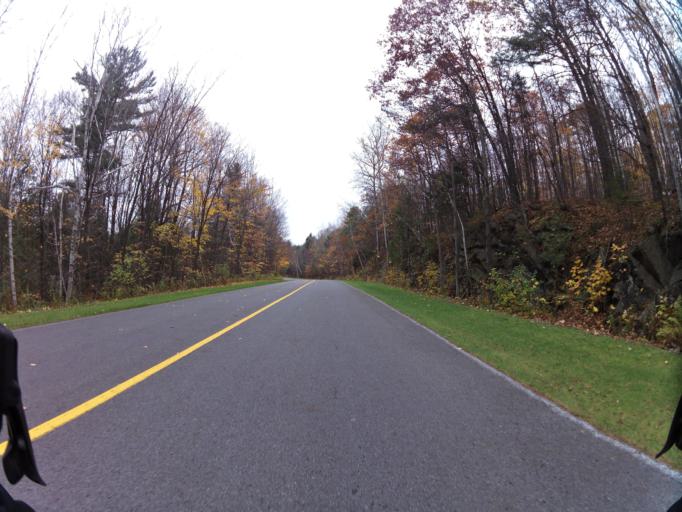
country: CA
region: Quebec
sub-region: Outaouais
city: Gatineau
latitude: 45.5045
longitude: -75.8223
